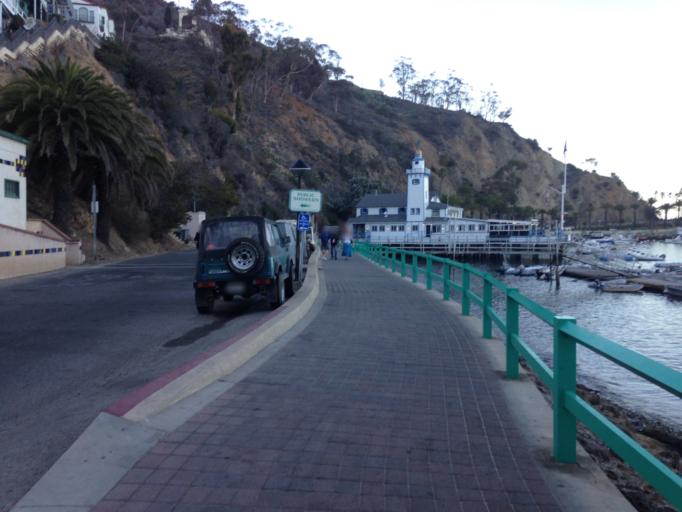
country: US
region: California
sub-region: Los Angeles County
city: Avalon
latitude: 33.3458
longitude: -118.3271
